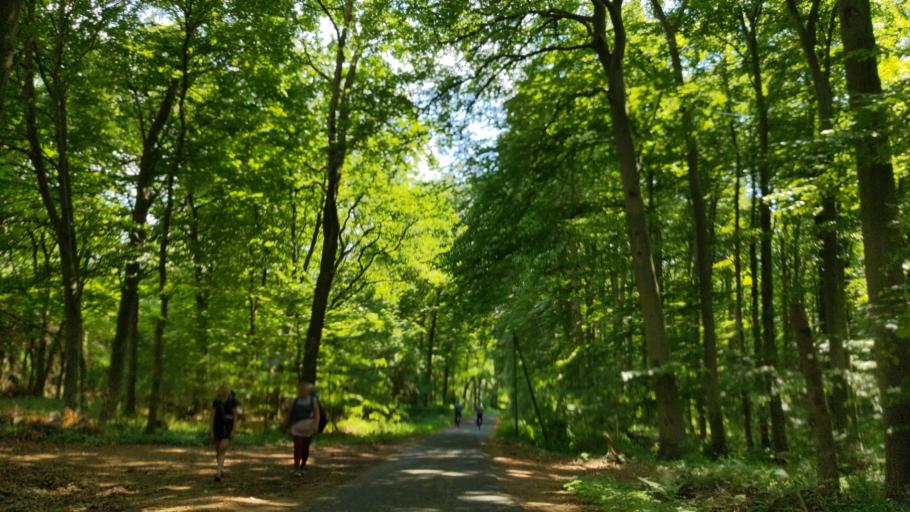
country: DE
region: Schleswig-Holstein
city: Buchholz
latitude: 53.7365
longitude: 10.7682
